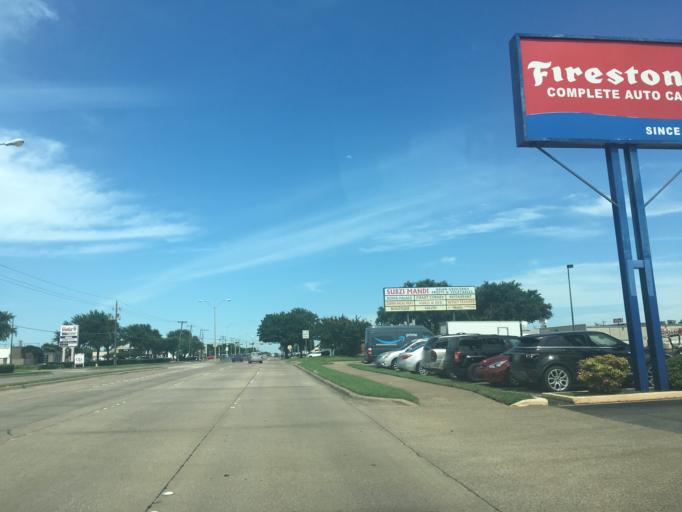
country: US
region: Texas
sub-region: Dallas County
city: Richardson
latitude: 32.9312
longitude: -96.7026
